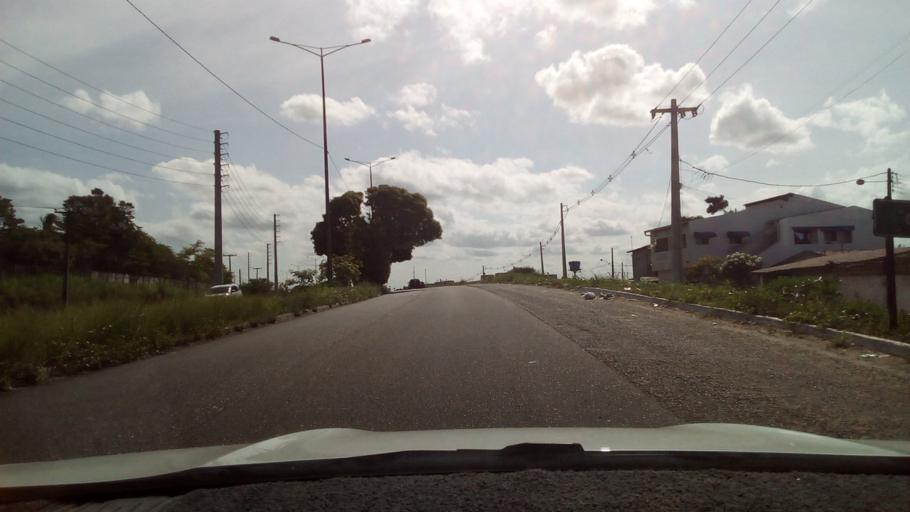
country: BR
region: Paraiba
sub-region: Bayeux
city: Bayeux
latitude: -7.1262
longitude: -34.8983
